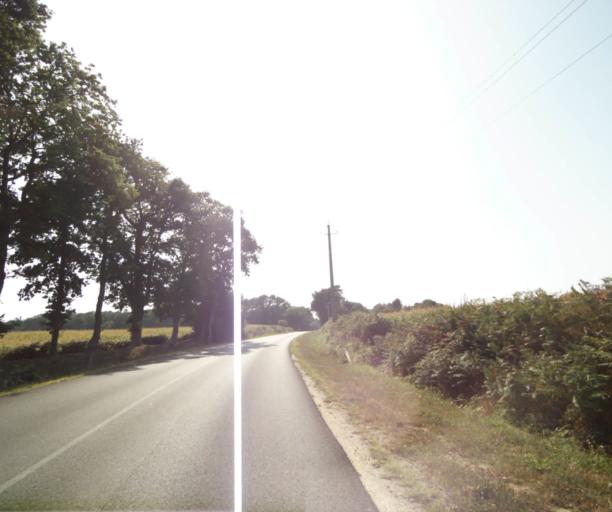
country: FR
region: Brittany
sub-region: Departement du Morbihan
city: Riantec
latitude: 47.7202
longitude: -3.2772
